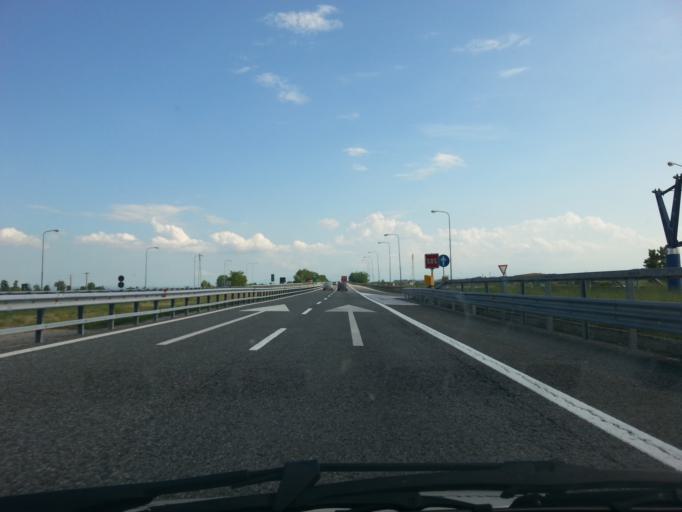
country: IT
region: Piedmont
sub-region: Provincia di Cuneo
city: Marene
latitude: 44.7036
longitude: 7.7631
